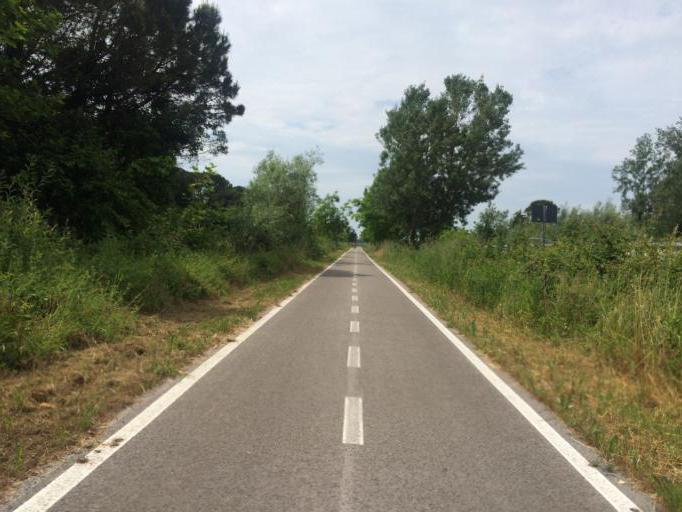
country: IT
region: Friuli Venezia Giulia
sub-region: Provincia di Udine
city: Aquileia
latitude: 45.7279
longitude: 13.3877
